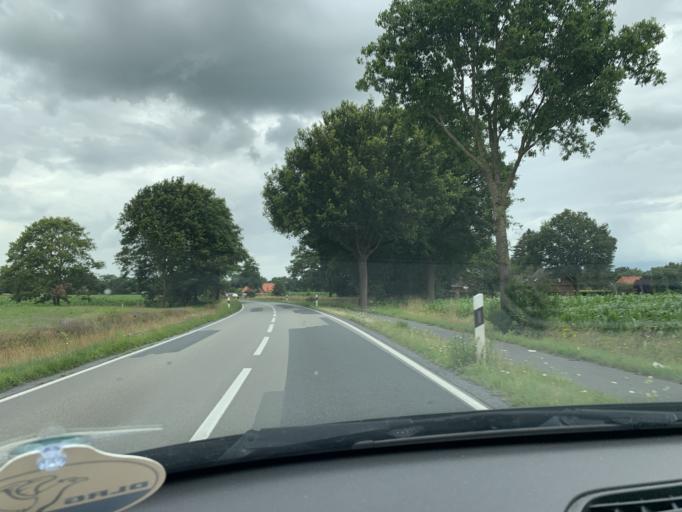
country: DE
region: Lower Saxony
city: Apen
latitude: 53.1427
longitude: 7.8765
